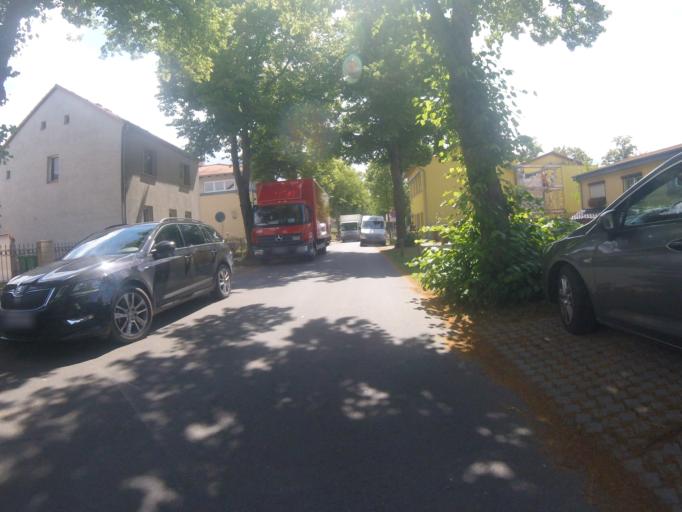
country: DE
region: Brandenburg
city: Bestensee
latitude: 52.2756
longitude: 13.6412
